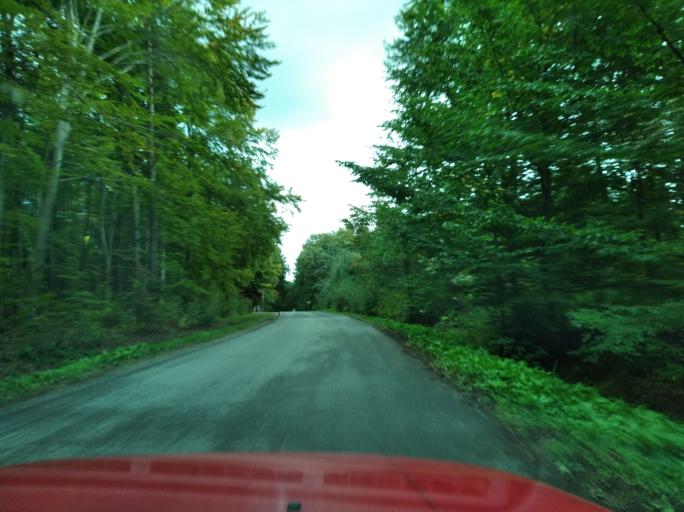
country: PL
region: Subcarpathian Voivodeship
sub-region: Powiat rzeszowski
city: Straszydle
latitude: 49.9321
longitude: 21.9924
